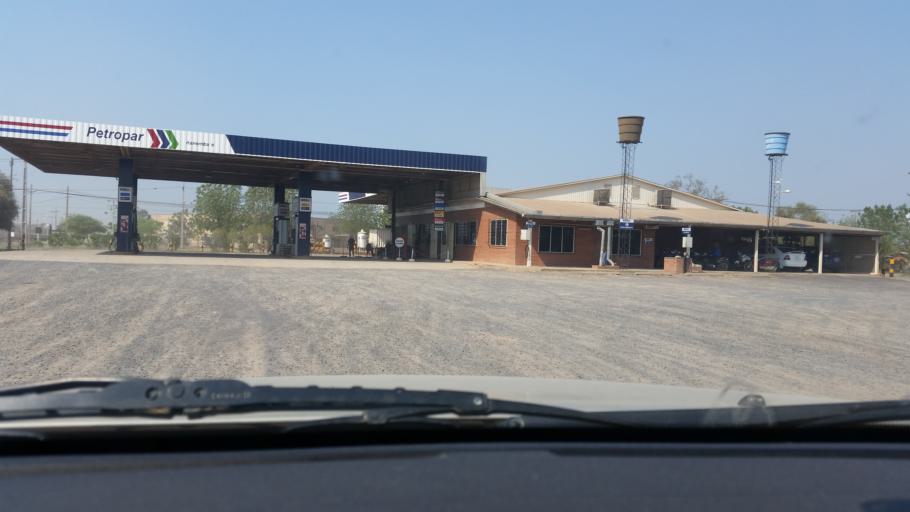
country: PY
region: Boqueron
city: Filadelfia
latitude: -22.3649
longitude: -60.0355
